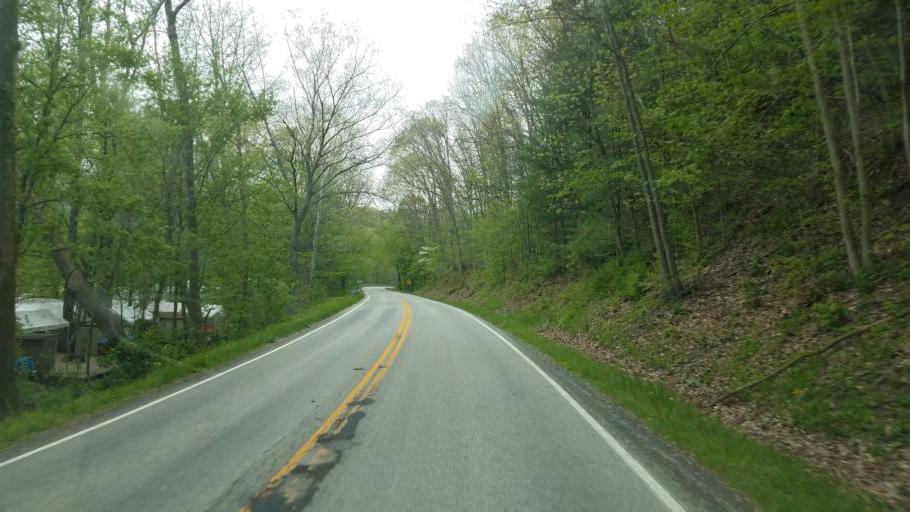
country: US
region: Ohio
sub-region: Ashland County
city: Loudonville
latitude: 40.6087
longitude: -82.2493
